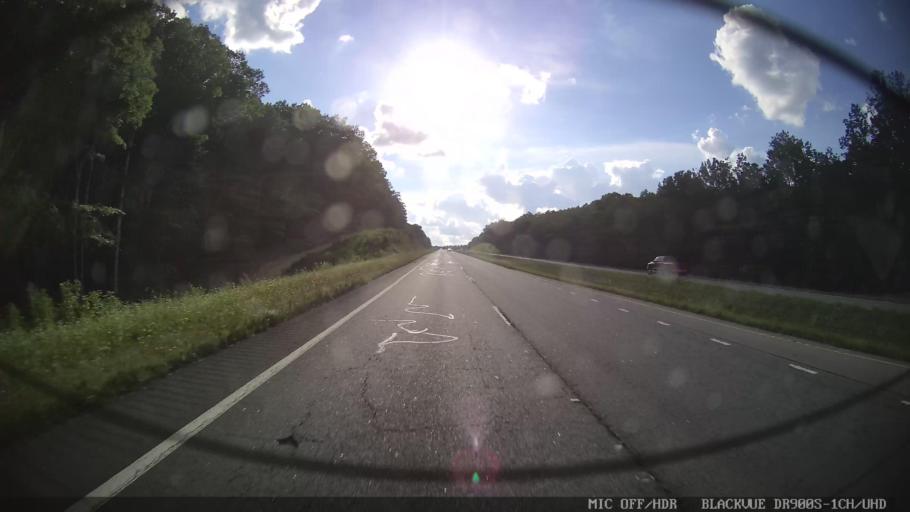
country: US
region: Georgia
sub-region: Bartow County
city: Euharlee
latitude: 34.2022
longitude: -85.0066
